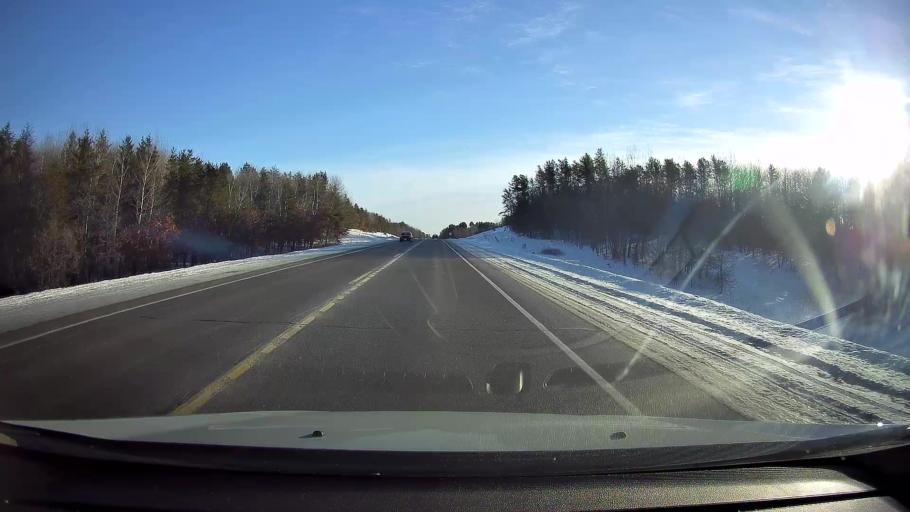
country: US
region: Wisconsin
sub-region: Washburn County
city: Spooner
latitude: 45.9104
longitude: -91.7889
